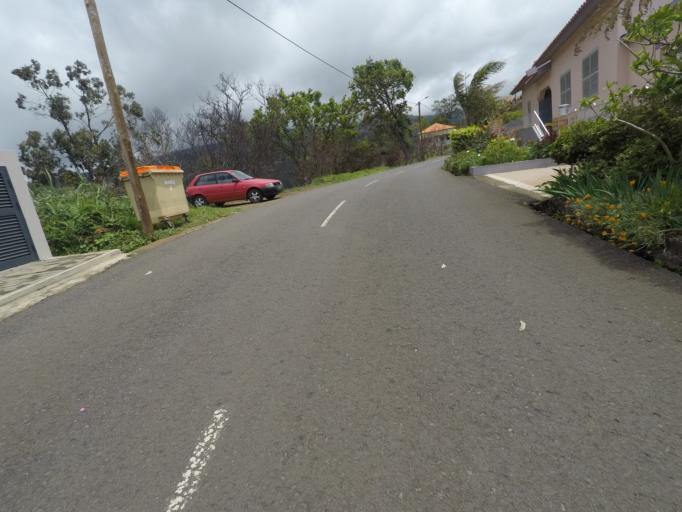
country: PT
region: Madeira
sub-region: Calheta
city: Faja da Ovelha
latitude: 32.7538
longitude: -17.2141
